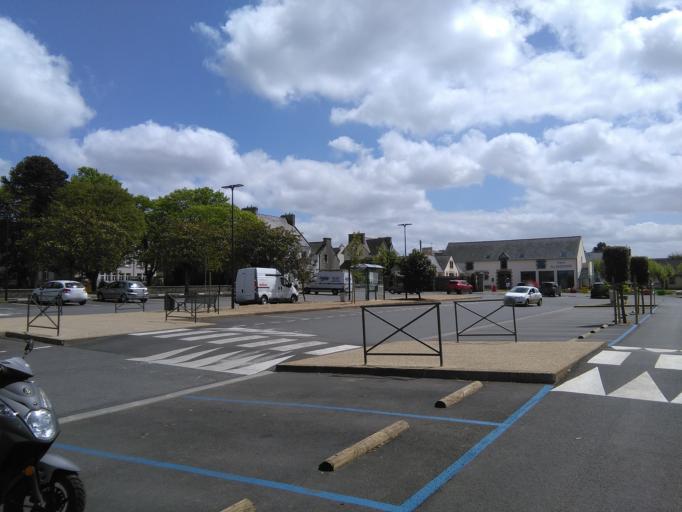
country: FR
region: Brittany
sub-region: Departement du Finistere
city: Landivisiau
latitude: 48.5103
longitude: -4.0688
